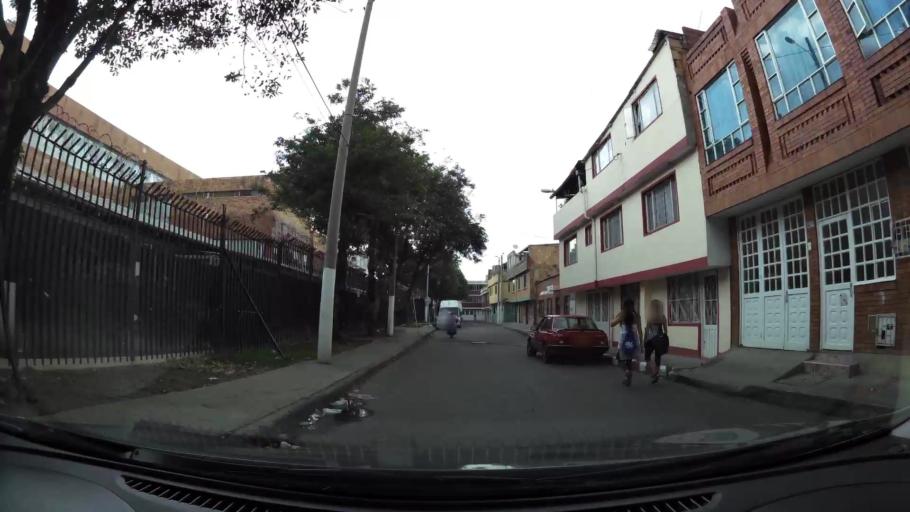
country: CO
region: Cundinamarca
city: La Calera
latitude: 4.7426
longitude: -74.0341
